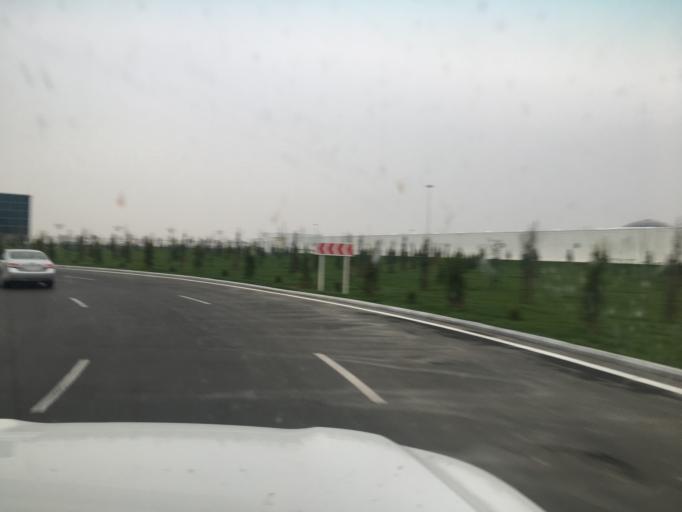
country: TM
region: Lebap
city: Turkmenabat
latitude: 38.9385
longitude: 63.5674
